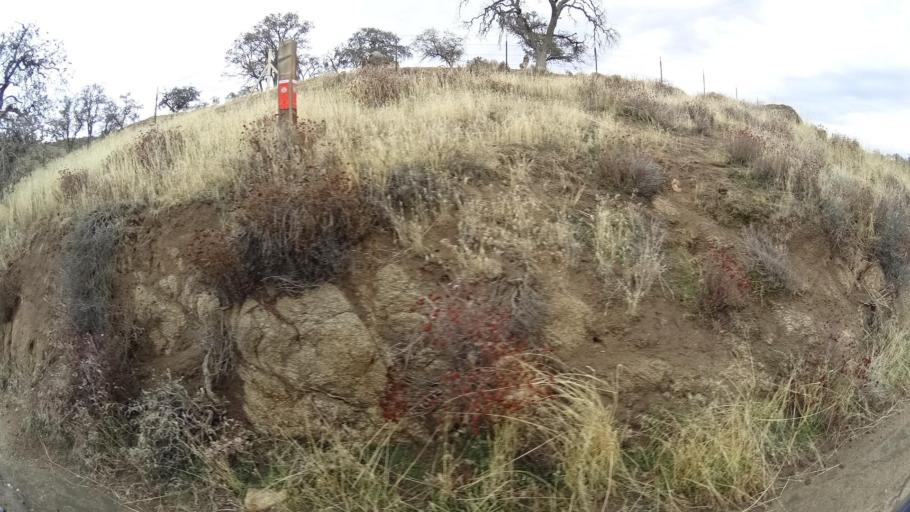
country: US
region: California
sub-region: Kern County
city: Stallion Springs
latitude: 35.1233
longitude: -118.7267
